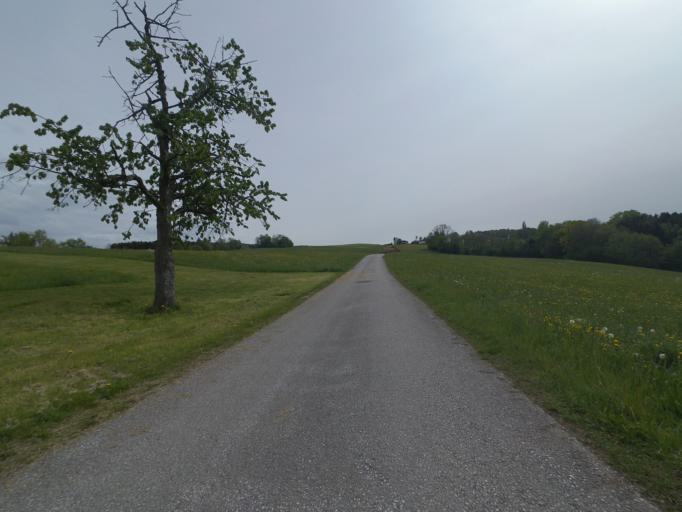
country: AT
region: Salzburg
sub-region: Politischer Bezirk Salzburg-Umgebung
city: Schleedorf
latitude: 47.9876
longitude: 13.1507
